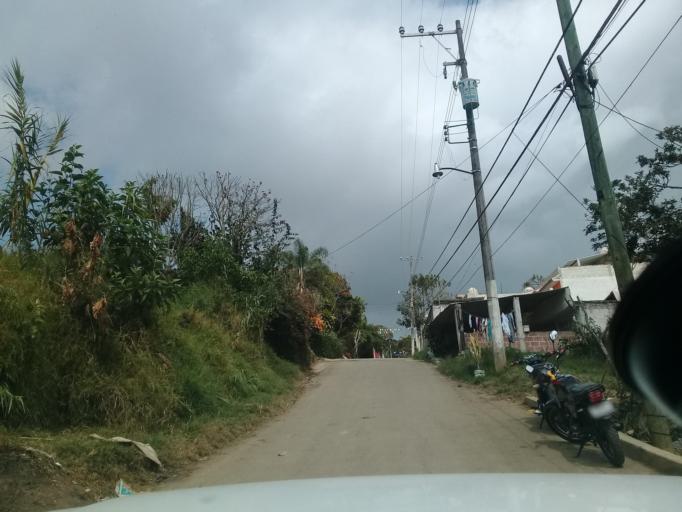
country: MX
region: Veracruz
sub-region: Xalapa
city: Fraccionamiento las Fuentes
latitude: 19.4761
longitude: -96.8764
